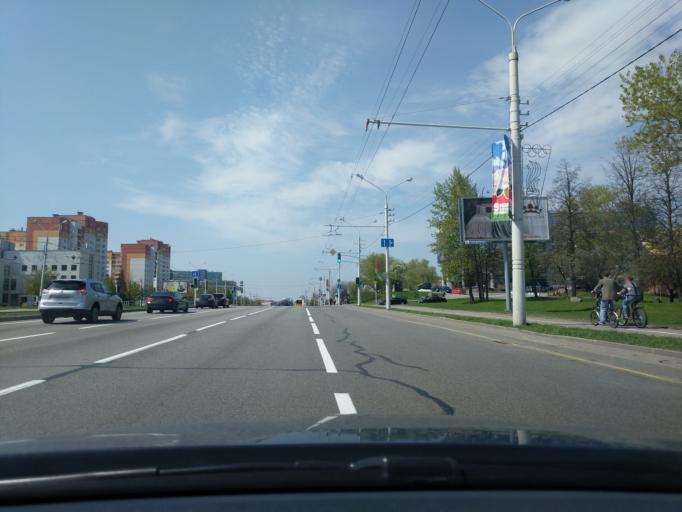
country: BY
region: Minsk
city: Minsk
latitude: 53.9337
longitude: 27.5037
